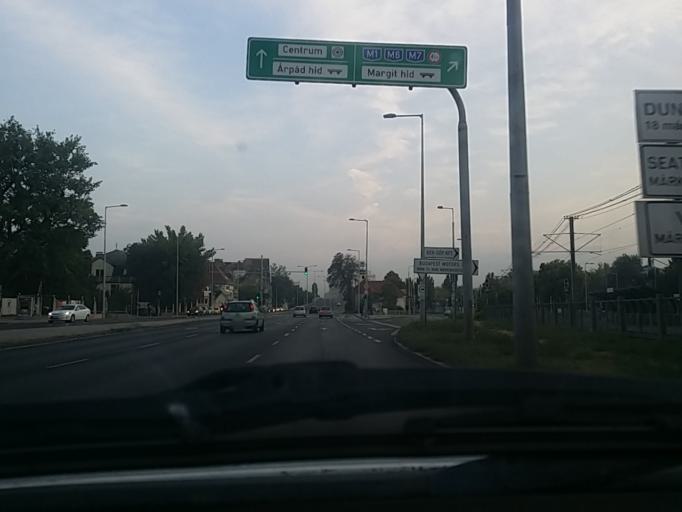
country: HU
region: Budapest
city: Budapest III. keruelet
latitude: 47.5577
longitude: 19.0460
